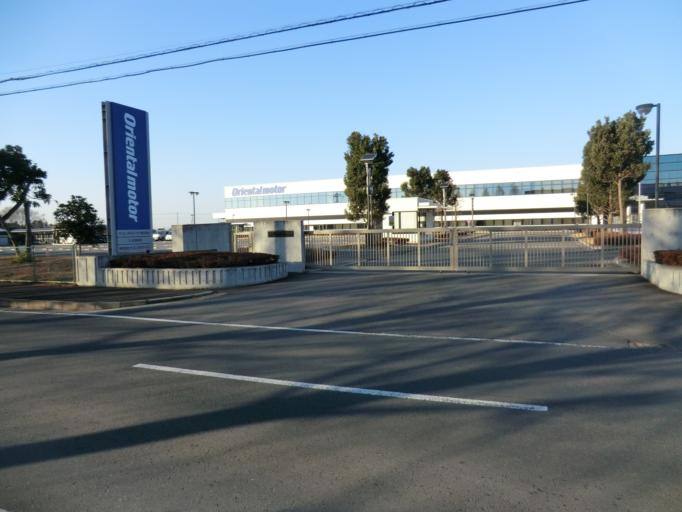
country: JP
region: Ibaraki
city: Ishige
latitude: 36.0875
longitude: 140.0649
